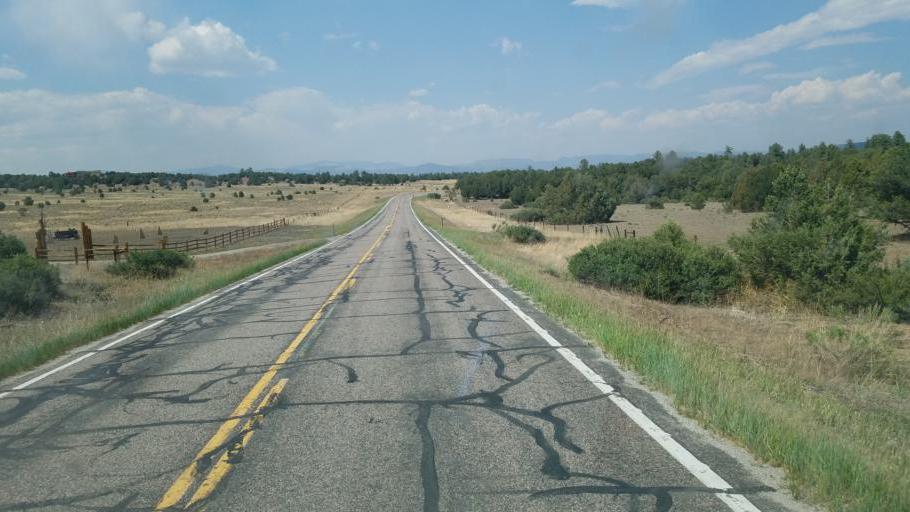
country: US
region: Colorado
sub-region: Custer County
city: Westcliffe
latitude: 38.3112
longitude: -105.6201
